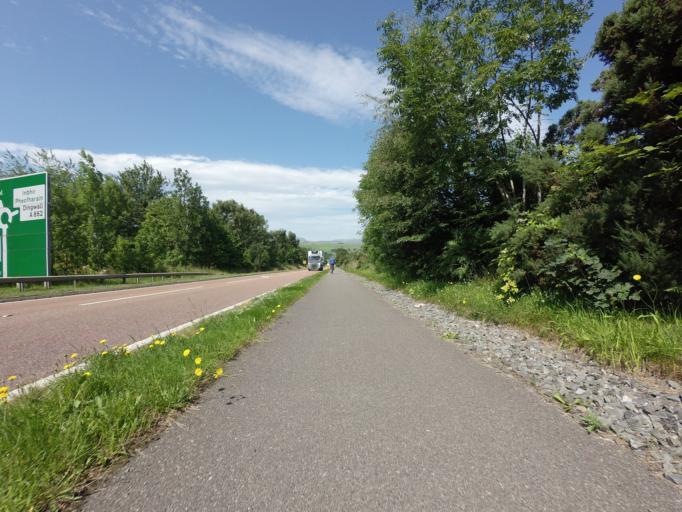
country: GB
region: Scotland
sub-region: Highland
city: Conon Bridge
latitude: 57.5680
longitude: -4.4252
